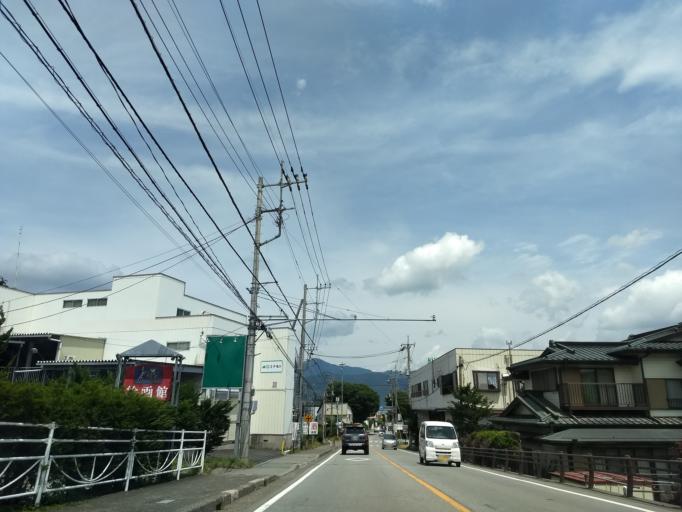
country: JP
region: Yamanashi
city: Fujikawaguchiko
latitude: 35.4649
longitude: 138.8026
